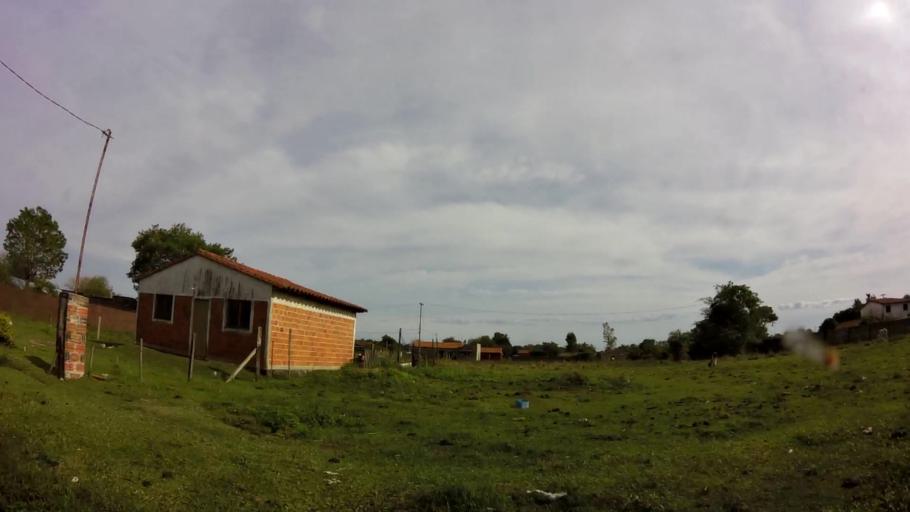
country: PY
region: Central
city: Limpio
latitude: -25.1717
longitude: -57.4920
